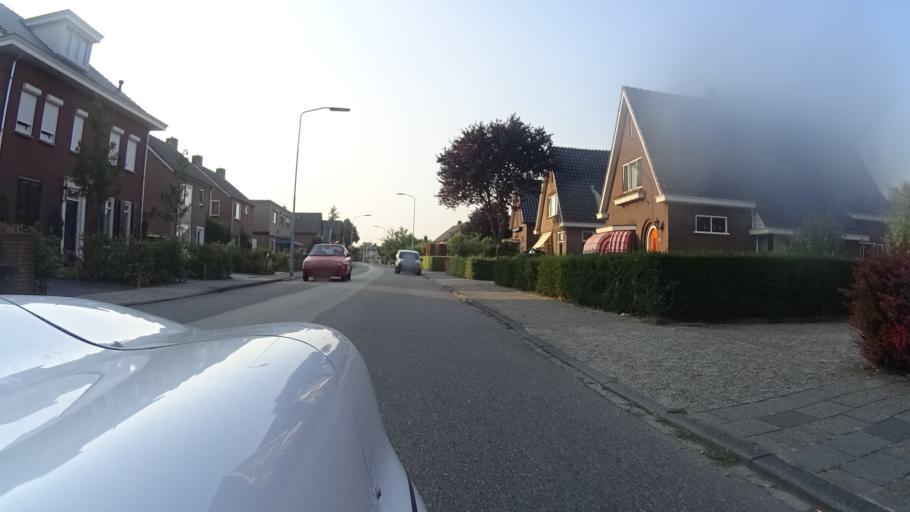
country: NL
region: Gelderland
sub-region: Gemeente Buren
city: Lienden
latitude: 51.8788
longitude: 5.5110
